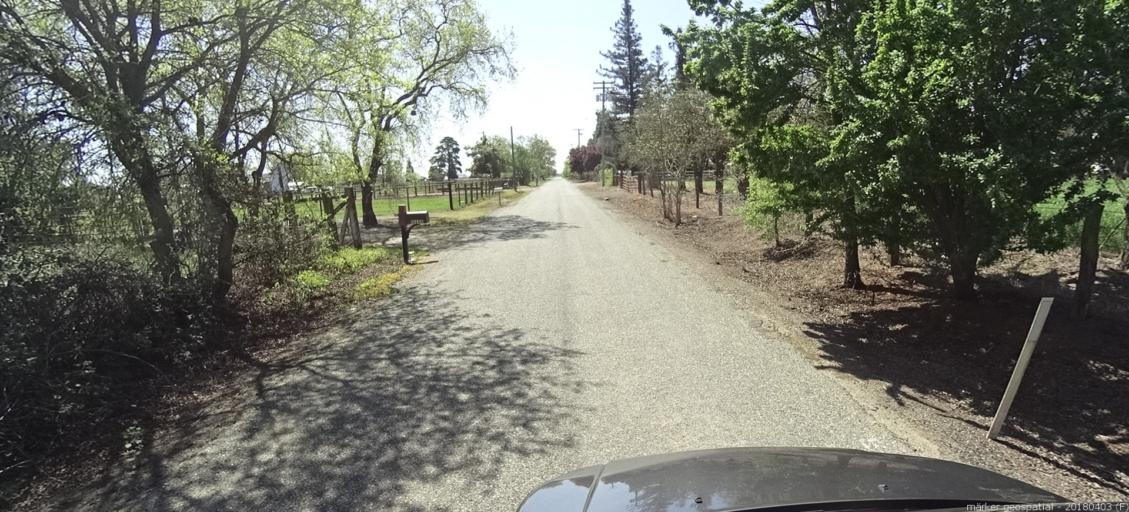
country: US
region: California
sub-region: Sacramento County
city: Wilton
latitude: 38.3992
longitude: -121.2874
